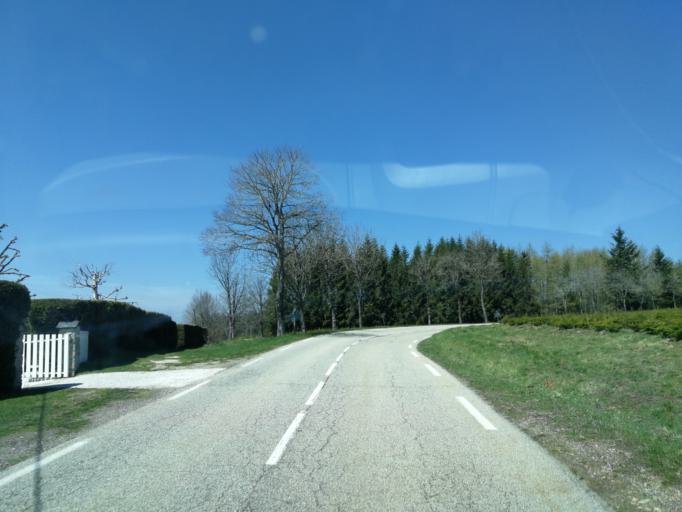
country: FR
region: Rhone-Alpes
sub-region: Departement de l'Ardeche
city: Saint-Agreve
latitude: 45.0694
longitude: 4.3841
